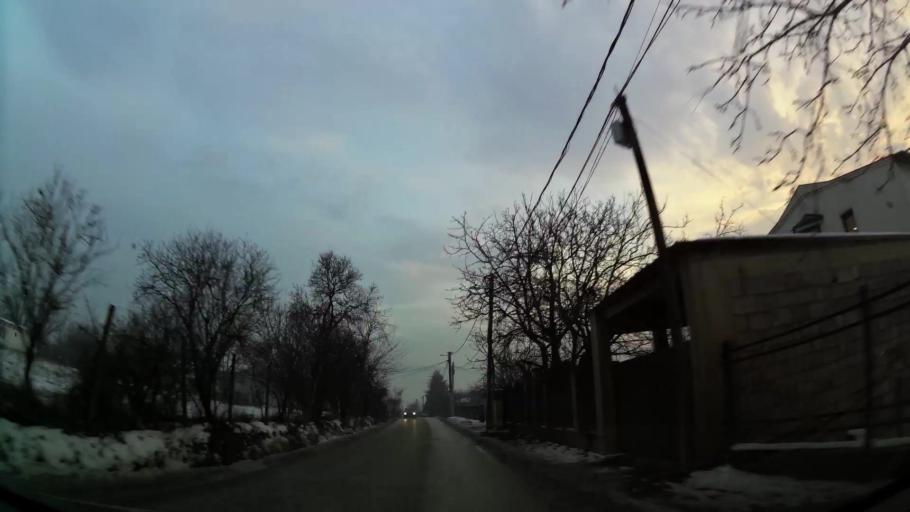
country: MK
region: Suto Orizari
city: Suto Orizare
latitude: 42.0324
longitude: 21.4074
